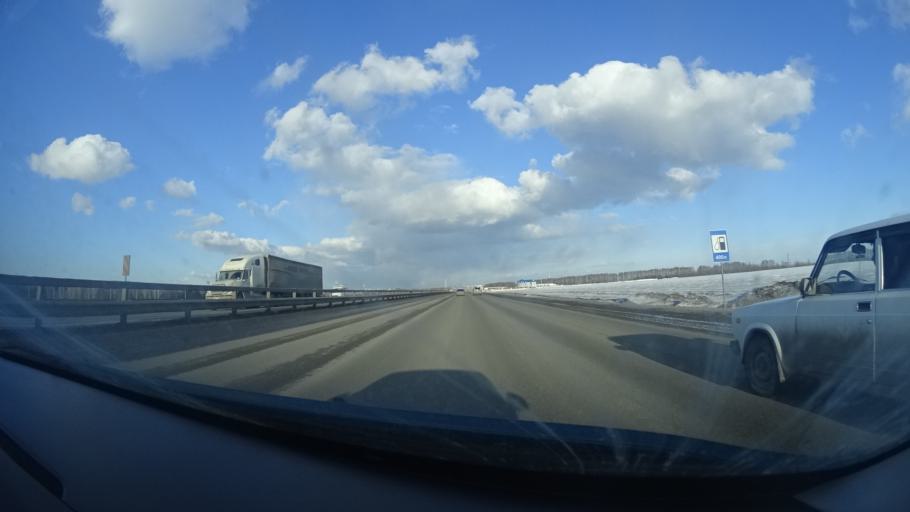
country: RU
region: Bashkortostan
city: Avdon
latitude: 54.6714
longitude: 55.7717
